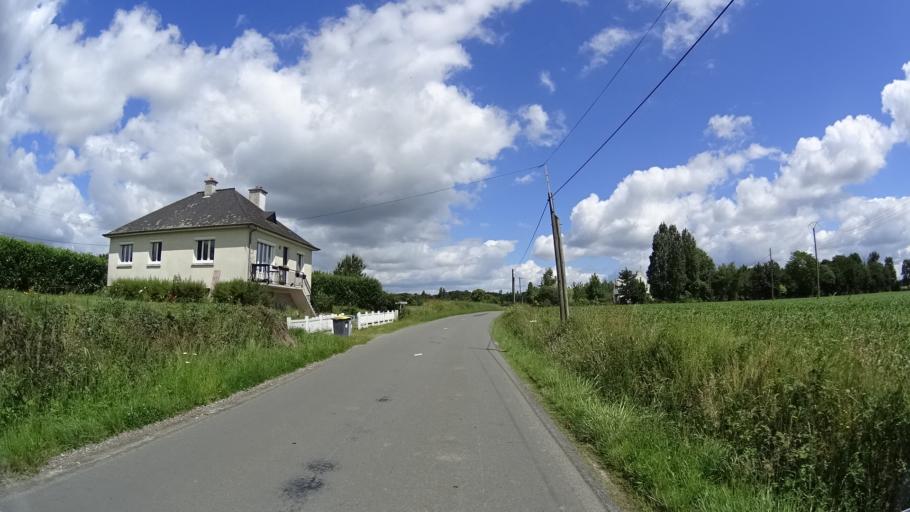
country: FR
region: Brittany
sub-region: Departement d'Ille-et-Vilaine
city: Saint-Gilles
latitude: 48.1663
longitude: -1.8301
